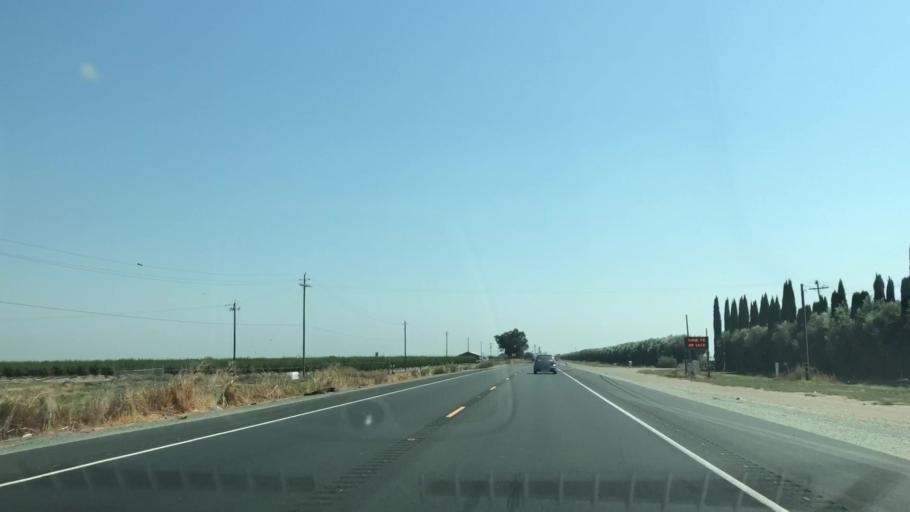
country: US
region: California
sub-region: San Joaquin County
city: Thornton
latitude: 38.1154
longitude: -121.4479
